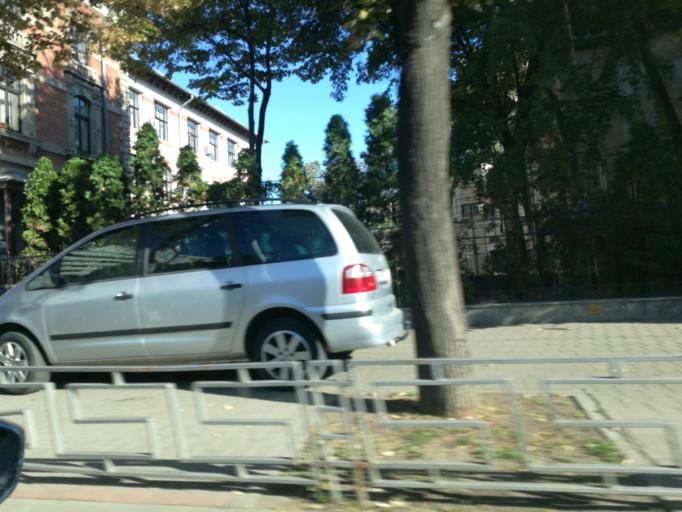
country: RO
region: Iasi
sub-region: Municipiul Iasi
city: Iasi
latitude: 47.1662
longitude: 27.5788
